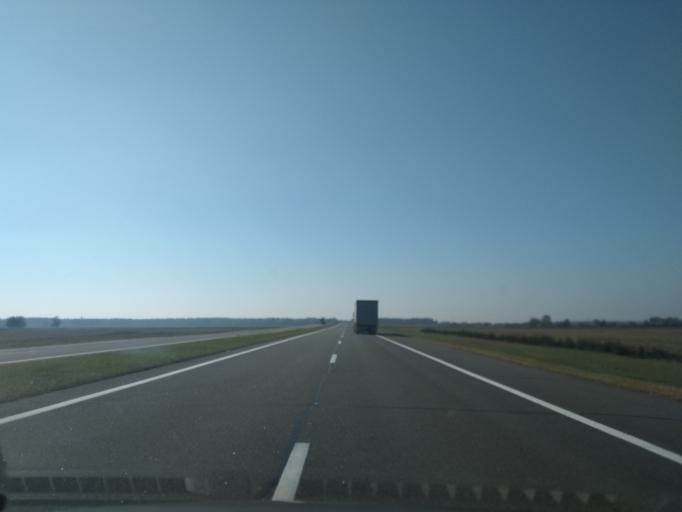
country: BY
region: Brest
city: Ivatsevichy
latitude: 52.7314
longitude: 25.4558
